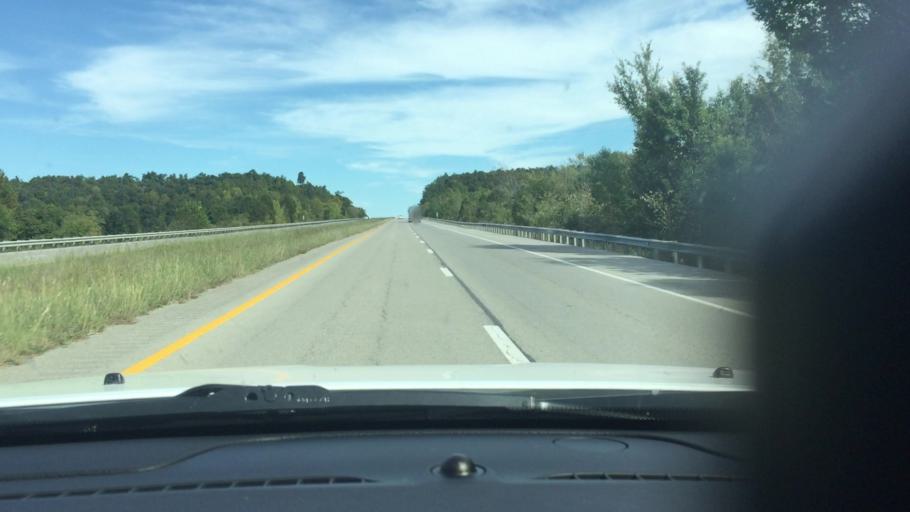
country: US
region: Kentucky
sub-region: Caldwell County
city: Princeton
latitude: 37.1397
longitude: -87.8428
